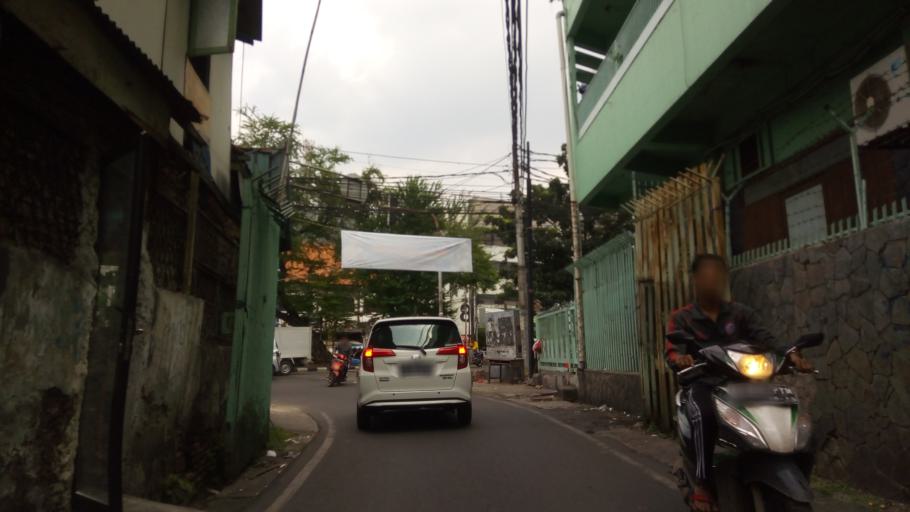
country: ID
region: Jakarta Raya
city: Jakarta
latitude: -6.1603
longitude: 106.8336
